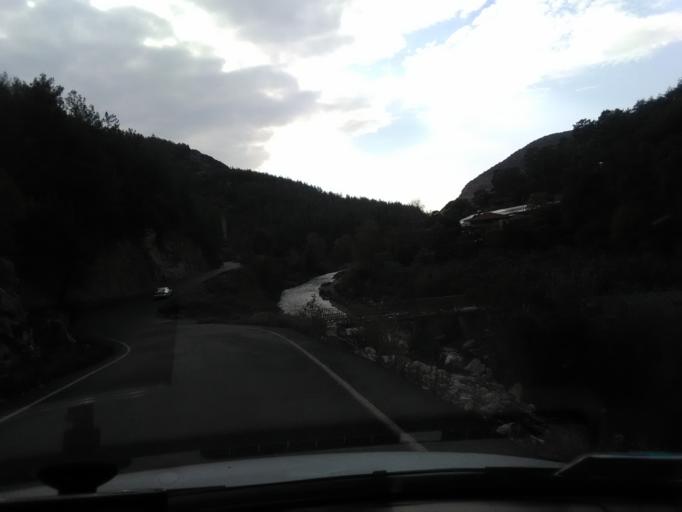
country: TR
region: Antalya
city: Gazipasa
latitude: 36.2871
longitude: 32.3749
